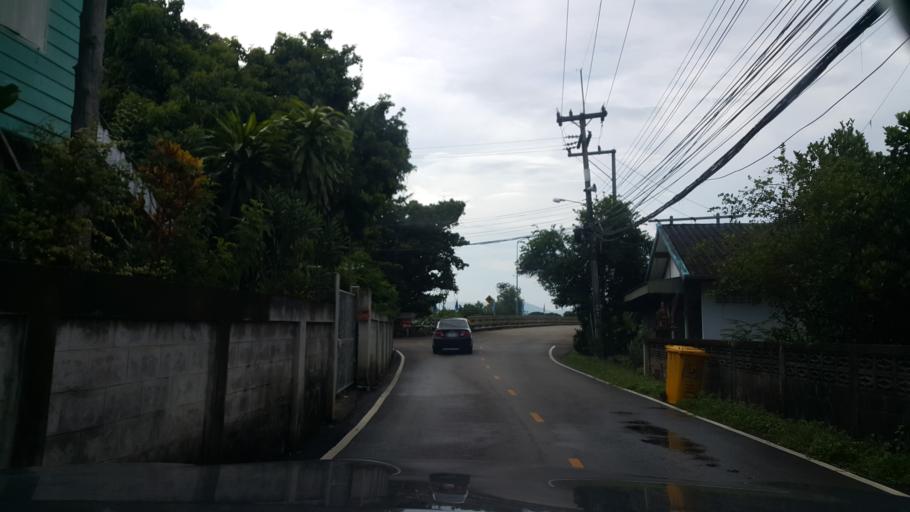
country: TH
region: Lampang
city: Thoen
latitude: 17.6070
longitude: 99.2193
